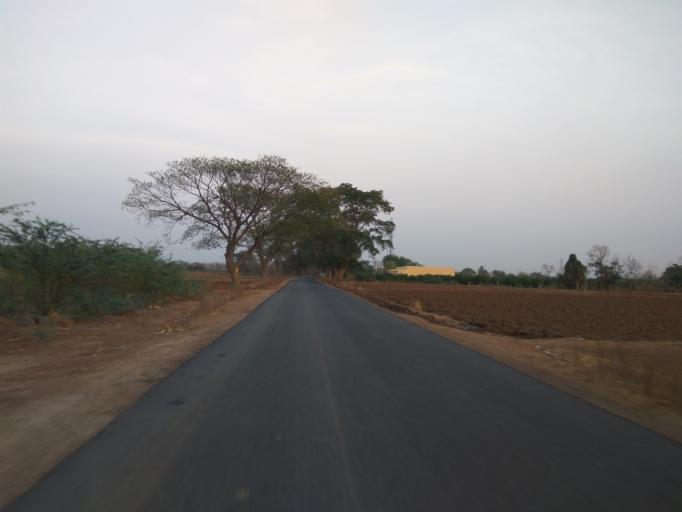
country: IN
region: Andhra Pradesh
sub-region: Prakasam
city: Markapur
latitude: 15.7489
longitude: 79.2313
